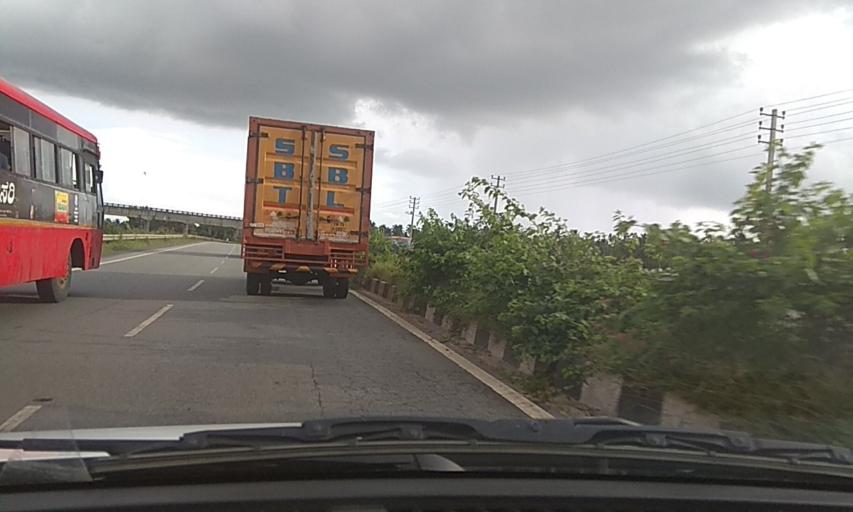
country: IN
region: Karnataka
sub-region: Mysore
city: Mysore
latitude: 12.2501
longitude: 76.6588
